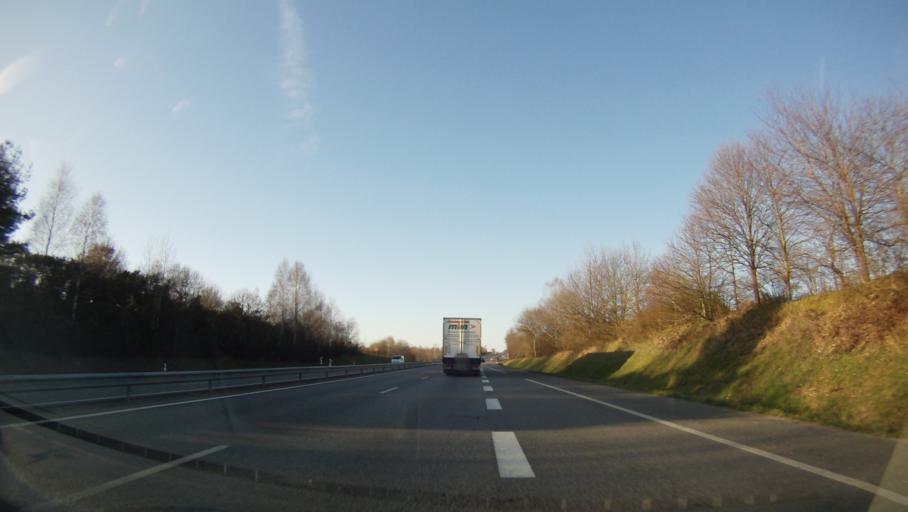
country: FR
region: Brittany
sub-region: Departement d'Ille-et-Vilaine
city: Crevin
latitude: 47.9390
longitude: -1.6750
